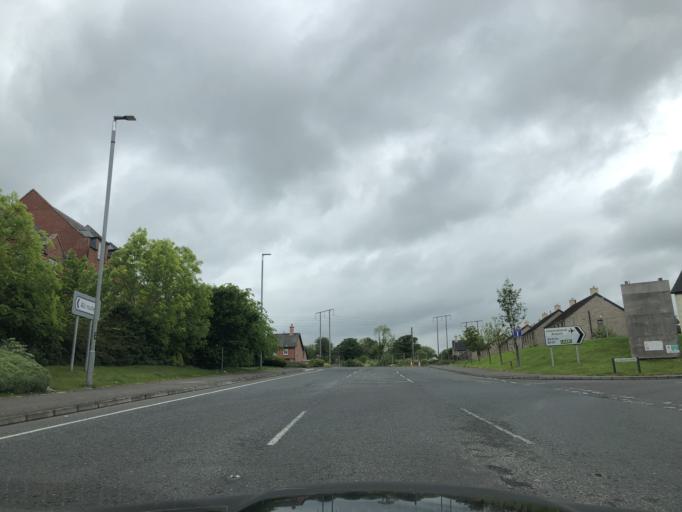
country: GB
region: Northern Ireland
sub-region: Lisburn District
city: Lisburn
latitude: 54.5304
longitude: -6.0731
